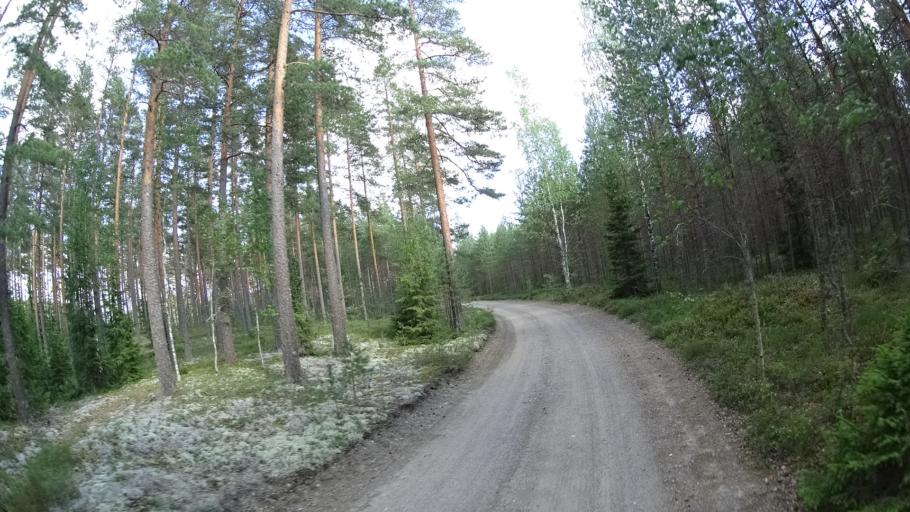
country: FI
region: Uusimaa
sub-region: Helsinki
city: Kaerkoelae
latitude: 60.7318
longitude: 24.0411
